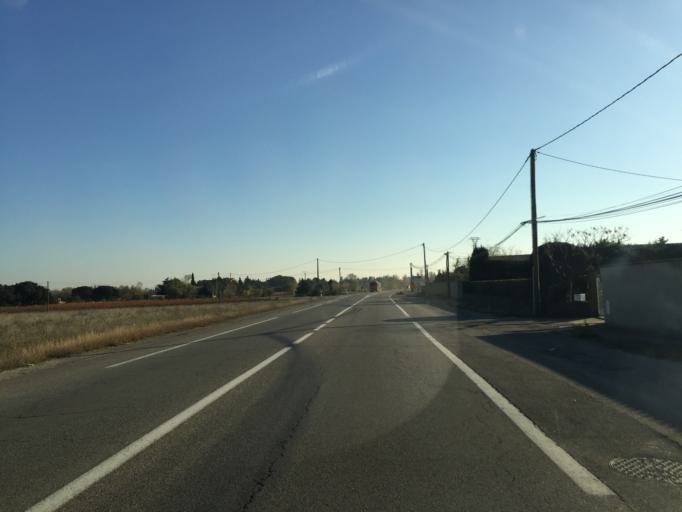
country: FR
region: Provence-Alpes-Cote d'Azur
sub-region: Departement du Vaucluse
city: Serignan-du-Comtat
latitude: 44.1803
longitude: 4.8557
